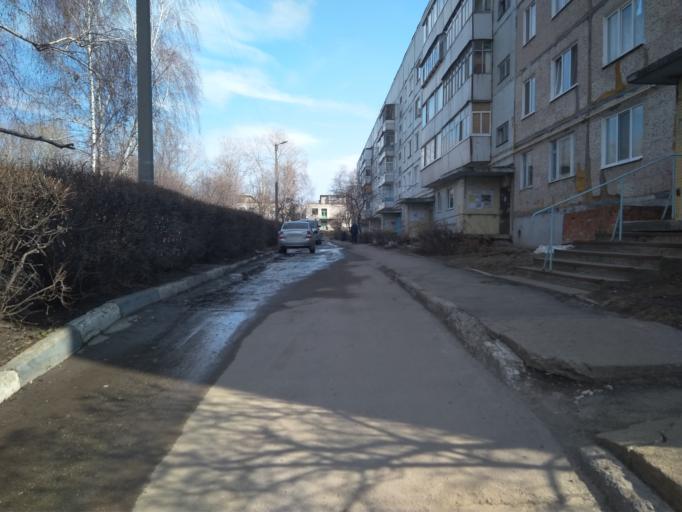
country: RU
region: Ulyanovsk
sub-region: Ulyanovskiy Rayon
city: Ulyanovsk
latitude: 54.2594
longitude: 48.3290
